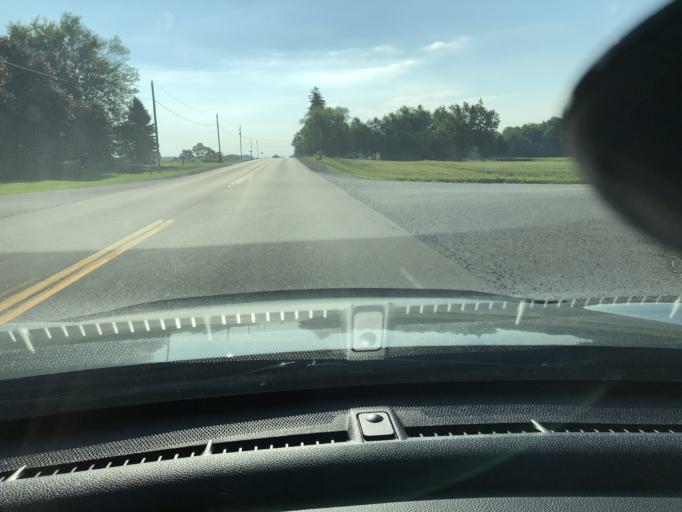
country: CA
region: Ontario
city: Stratford
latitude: 43.4243
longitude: -80.7881
